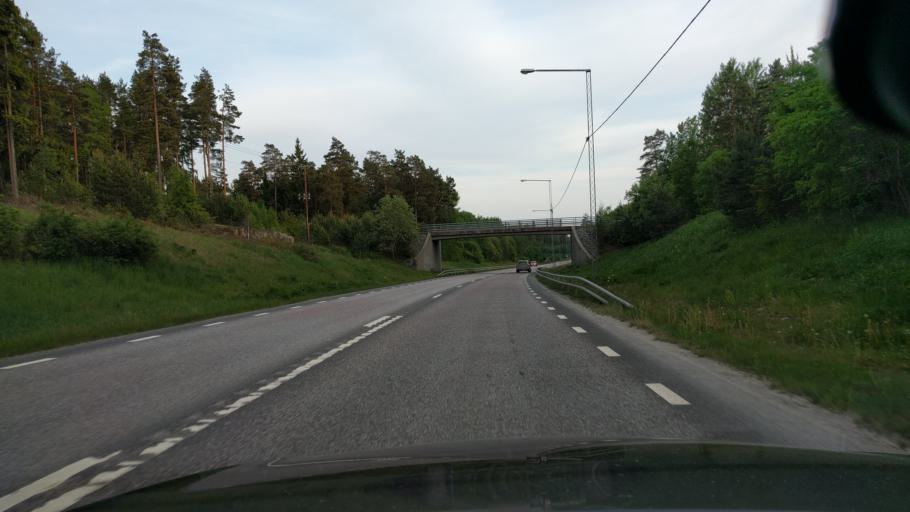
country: SE
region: Stockholm
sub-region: Vallentuna Kommun
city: Vallentuna
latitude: 59.5081
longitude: 18.0985
